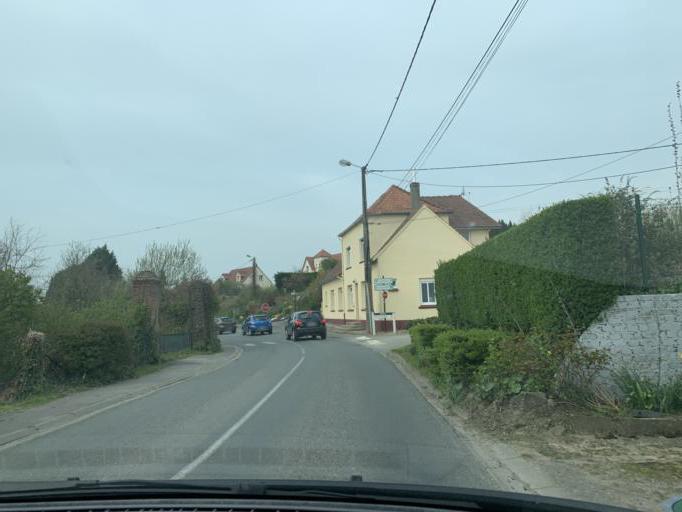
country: FR
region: Nord-Pas-de-Calais
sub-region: Departement du Pas-de-Calais
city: Montreuil
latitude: 50.4973
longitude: 1.7931
